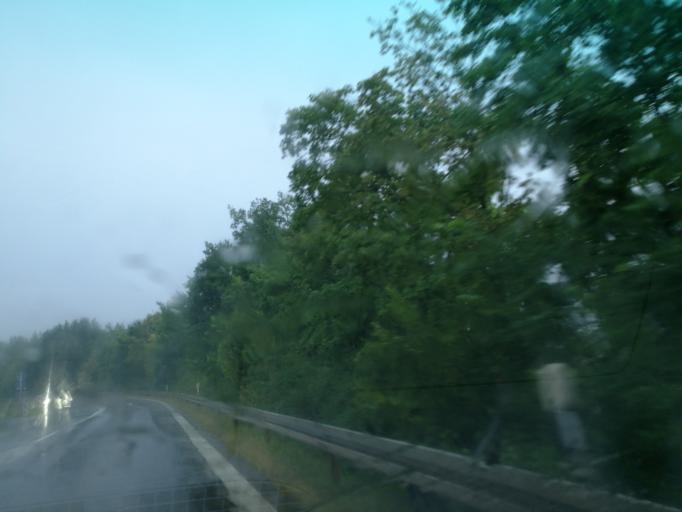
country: DE
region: Bavaria
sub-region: Regierungsbezirk Mittelfranken
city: Erlangen
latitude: 49.5414
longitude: 10.9947
